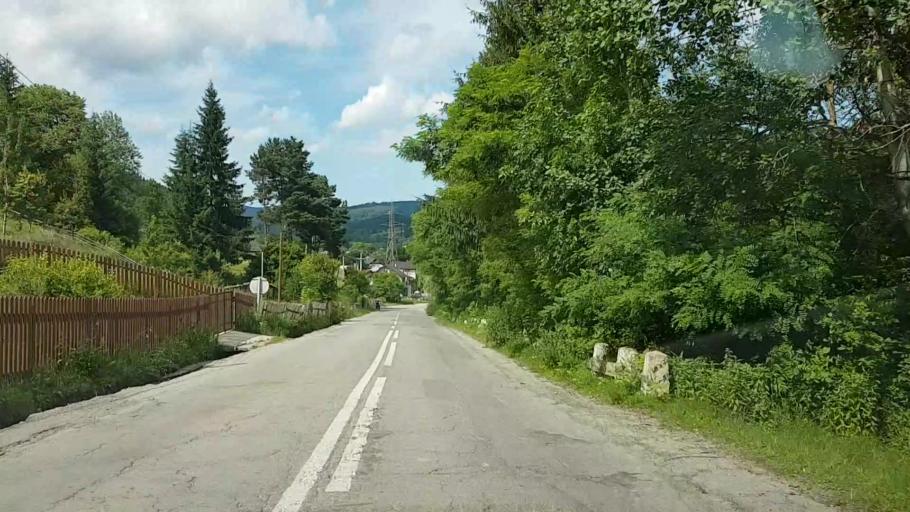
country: RO
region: Neamt
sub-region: Comuna Hangu
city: Hangu
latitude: 47.0584
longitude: 26.0320
